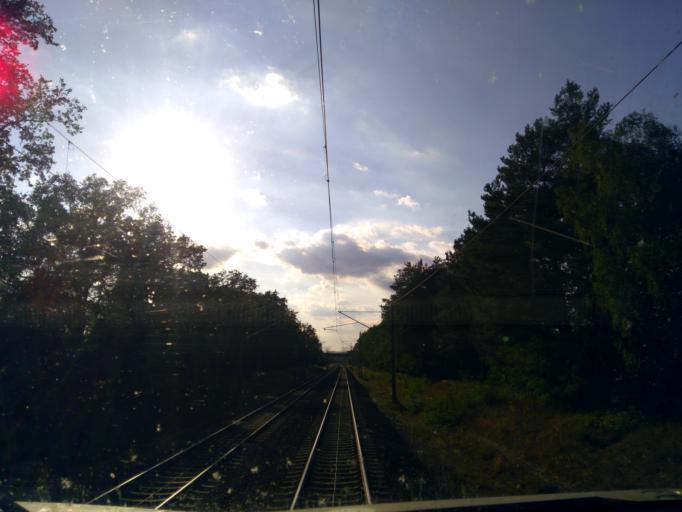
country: DE
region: Brandenburg
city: Ruhstadt
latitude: 52.9837
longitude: 11.8744
